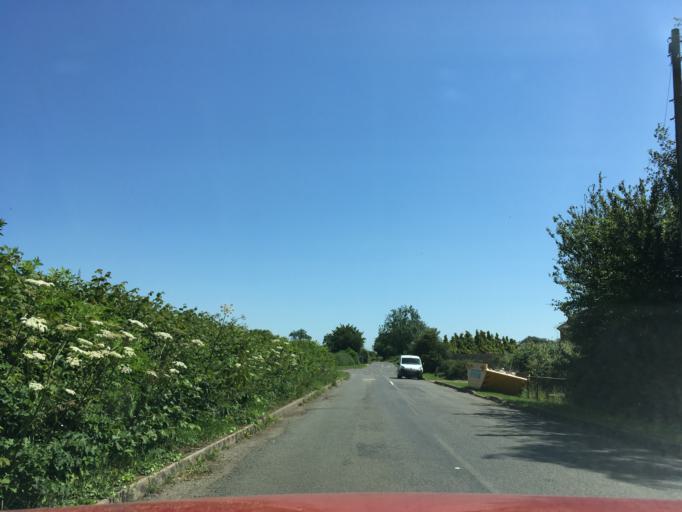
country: GB
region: England
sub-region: Milton Keynes
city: Calverton
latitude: 52.0034
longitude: -0.8676
